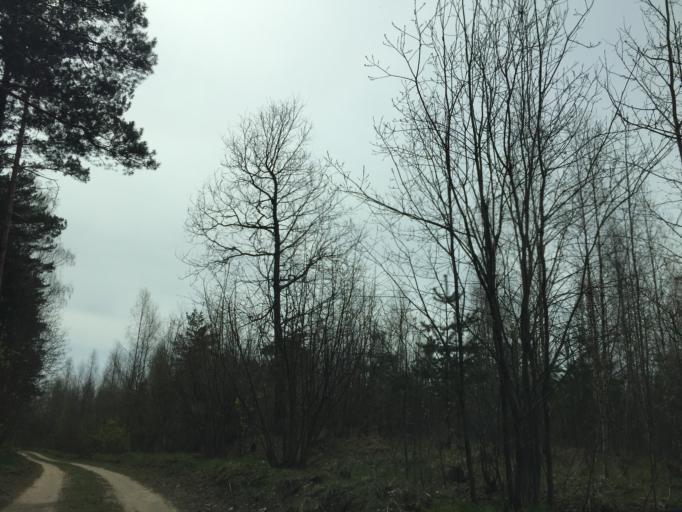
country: LV
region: Ludzas Rajons
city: Ludza
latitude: 56.5299
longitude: 27.5819
